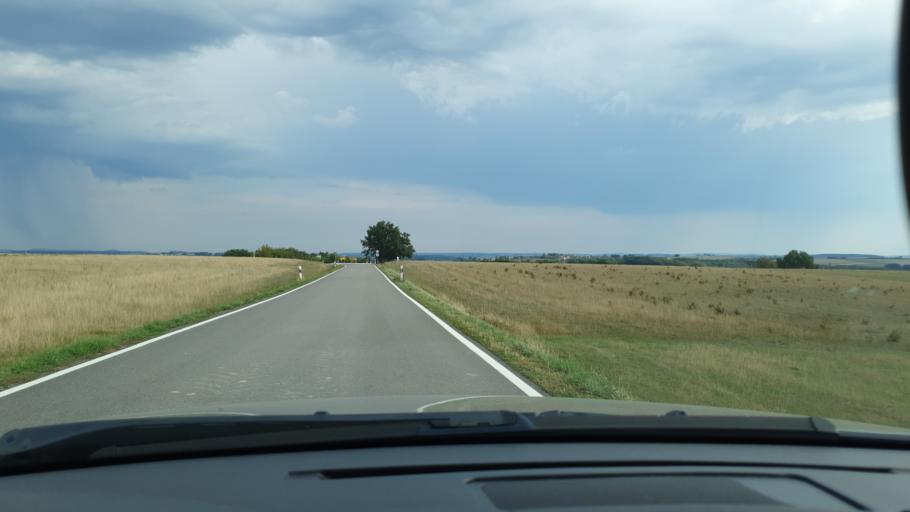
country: DE
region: Rheinland-Pfalz
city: Knopp-Labach
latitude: 49.3280
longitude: 7.4895
